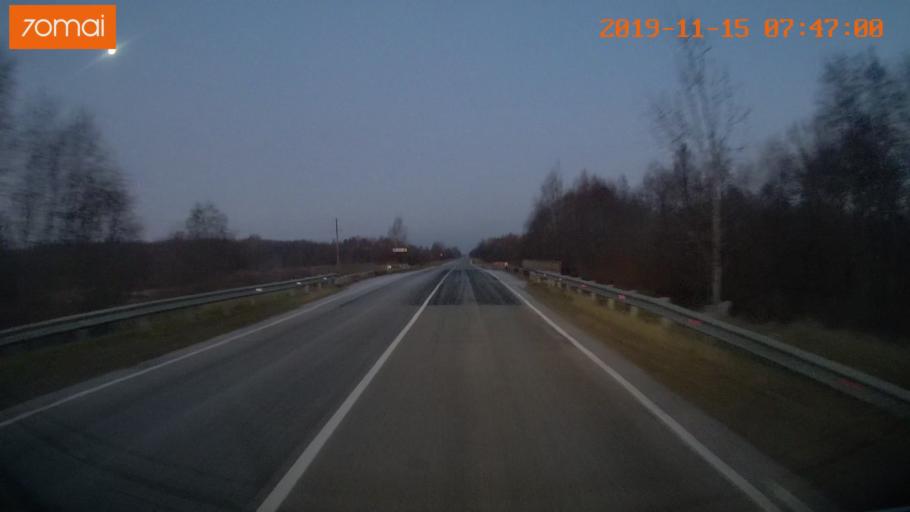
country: RU
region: Vologda
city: Sheksna
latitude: 58.8375
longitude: 38.2686
